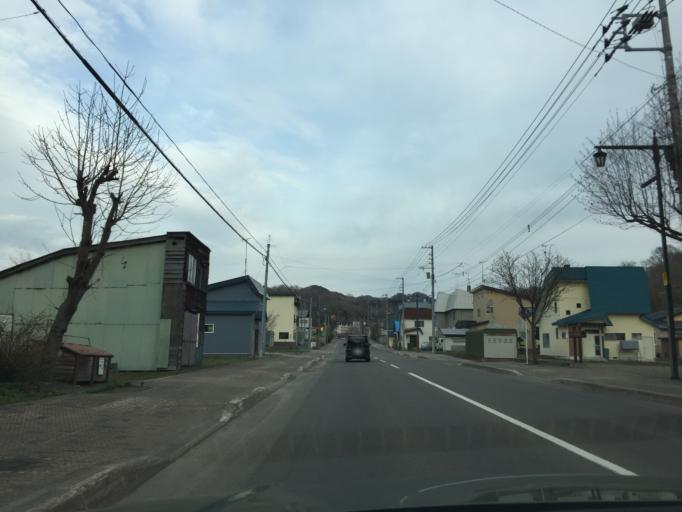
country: JP
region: Hokkaido
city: Utashinai
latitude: 43.5220
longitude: 142.0388
